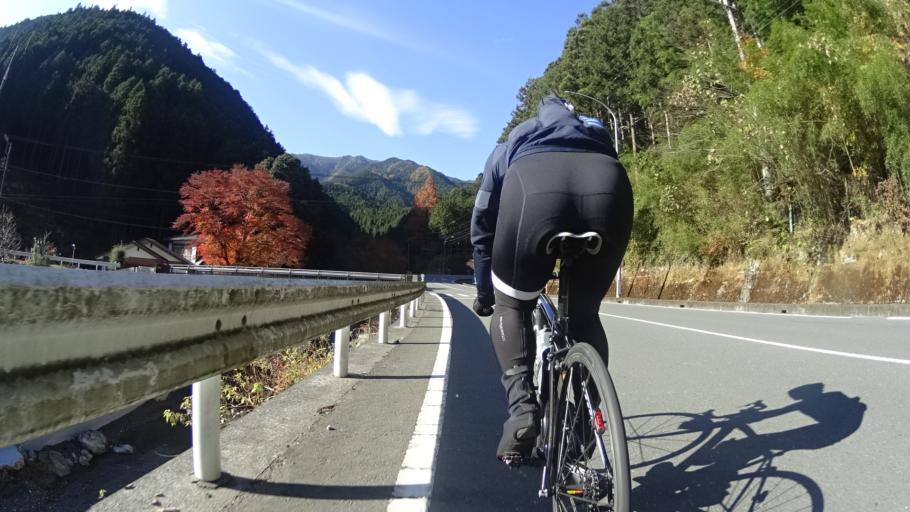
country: JP
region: Saitama
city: Chichibu
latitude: 35.9050
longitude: 139.1594
